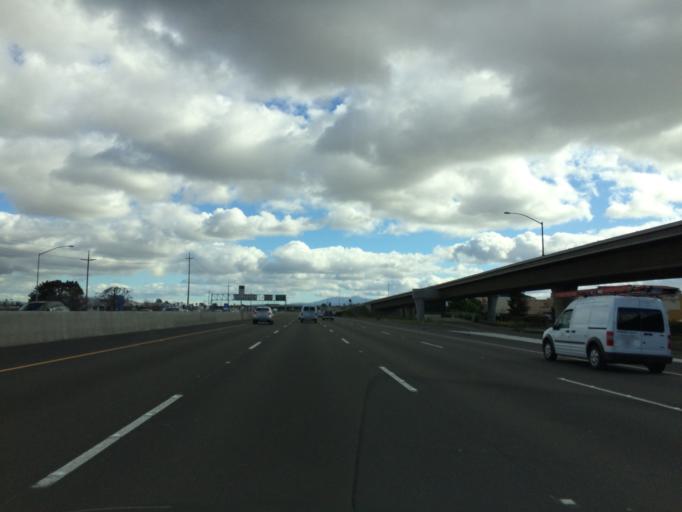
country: US
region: California
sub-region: Santa Clara County
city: Milpitas
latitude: 37.4226
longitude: -121.9156
